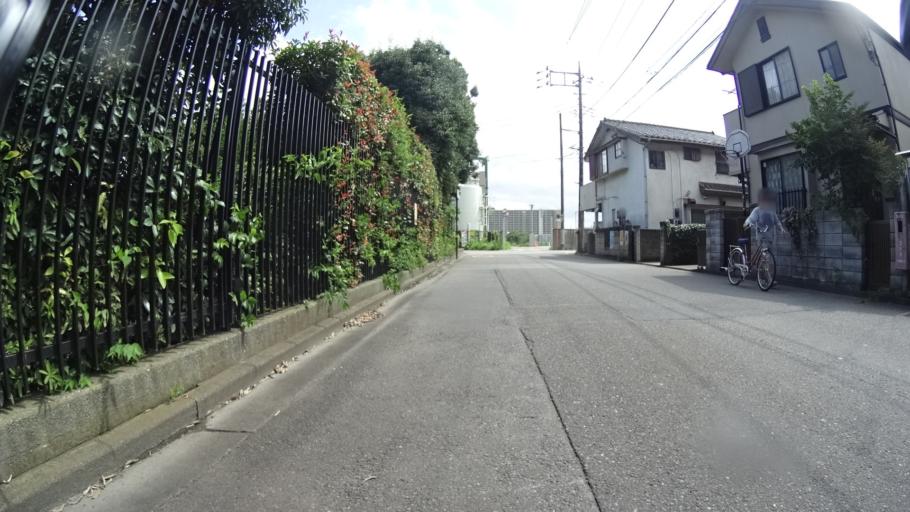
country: JP
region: Tokyo
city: Hino
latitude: 35.6868
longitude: 139.4106
